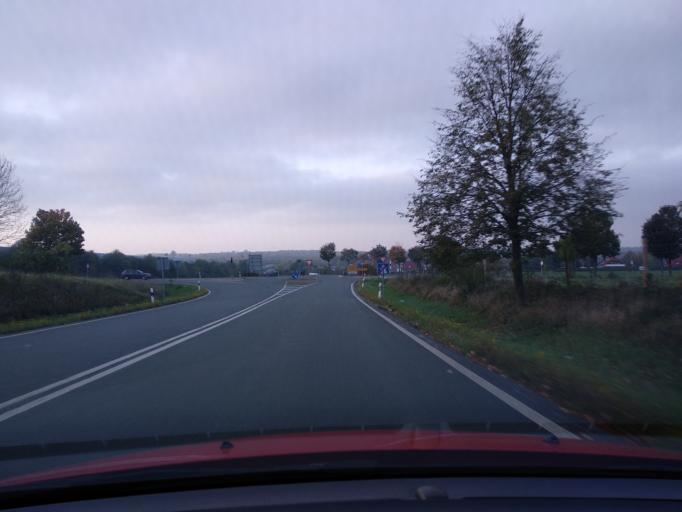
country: DE
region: North Rhine-Westphalia
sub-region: Regierungsbezirk Detmold
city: Paderborn
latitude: 51.6492
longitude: 8.7188
